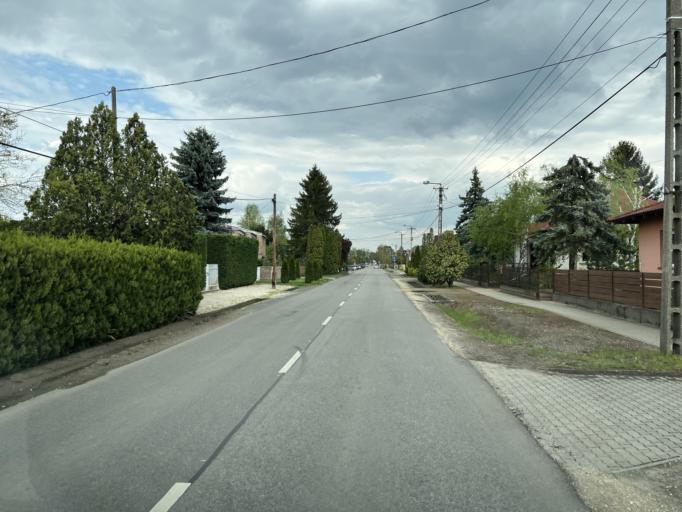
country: HU
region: Pest
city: Hernad
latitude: 47.1678
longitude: 19.4098
